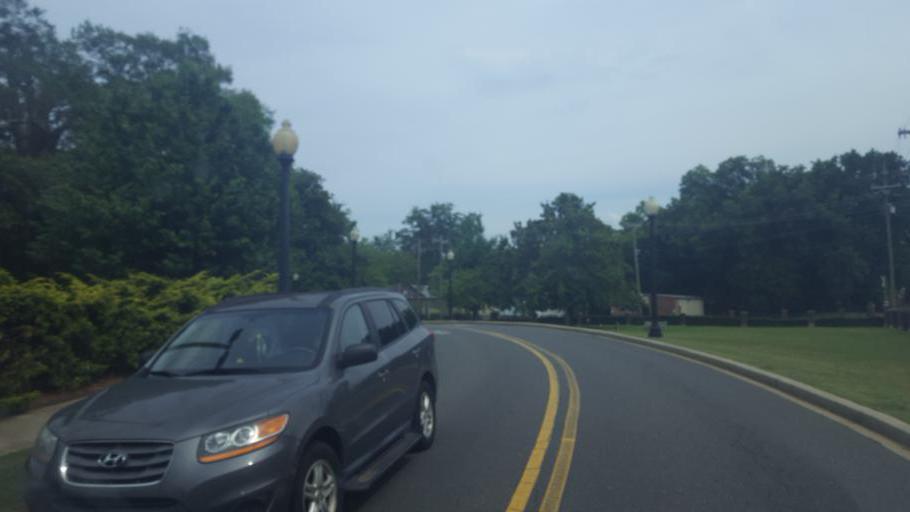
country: US
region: South Carolina
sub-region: York County
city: Rock Hill
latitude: 34.9363
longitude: -81.0318
